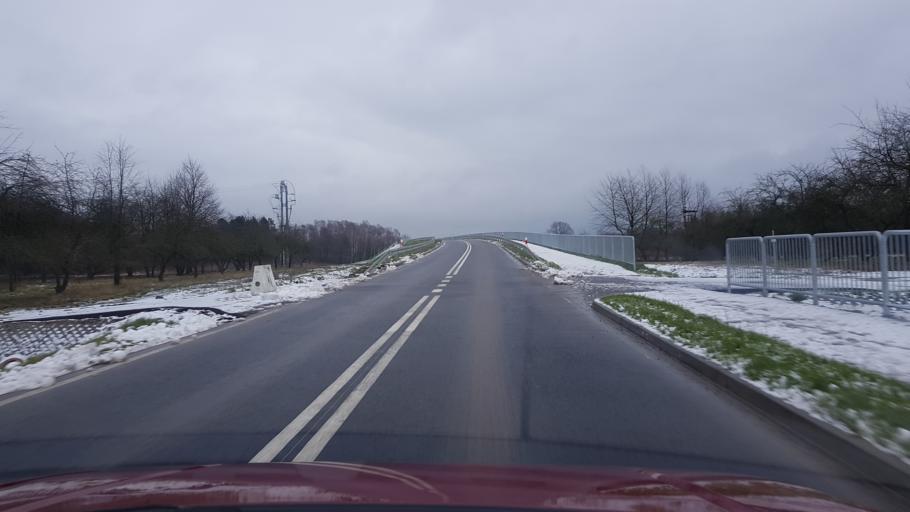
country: PL
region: West Pomeranian Voivodeship
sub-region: Powiat gryficki
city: Ploty
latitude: 53.8571
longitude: 15.3401
